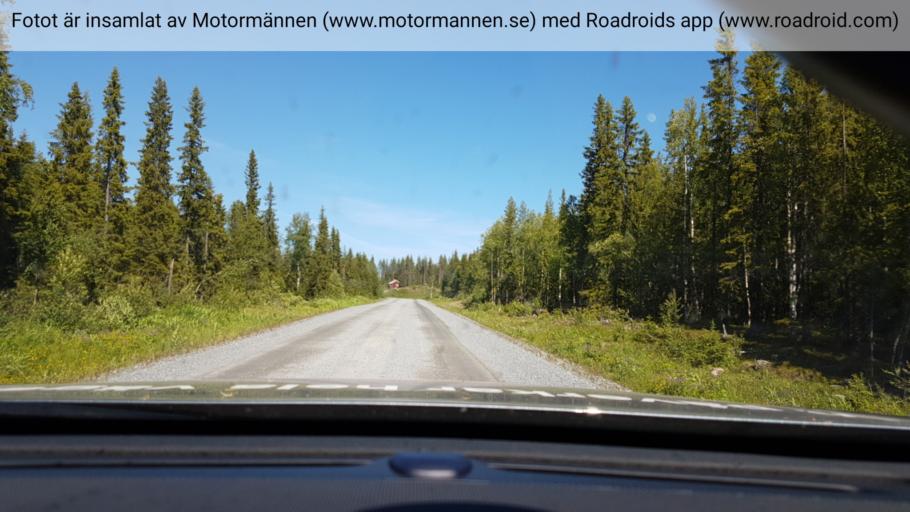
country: SE
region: Vaesterbotten
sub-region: Vilhelmina Kommun
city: Sjoberg
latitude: 64.6841
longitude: 15.7536
